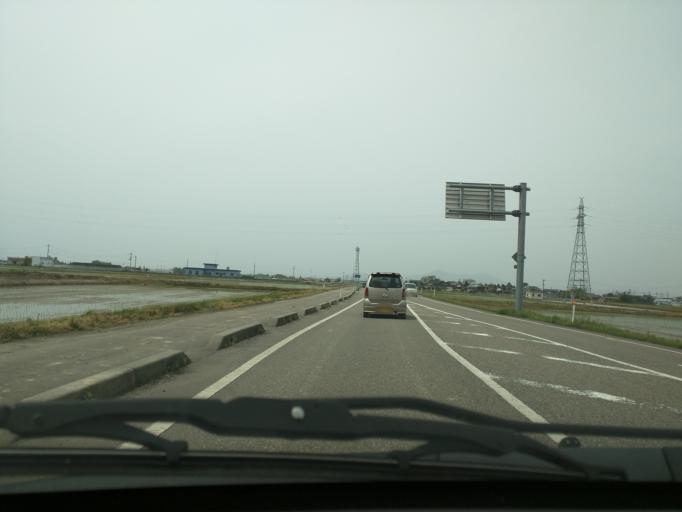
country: JP
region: Niigata
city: Mitsuke
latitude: 37.5732
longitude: 138.9449
